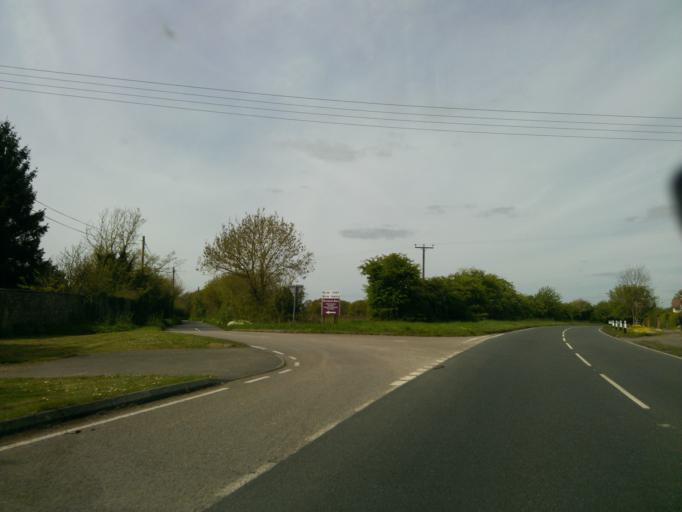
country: GB
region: England
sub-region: Essex
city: Earls Colne
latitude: 51.9303
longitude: 0.6718
